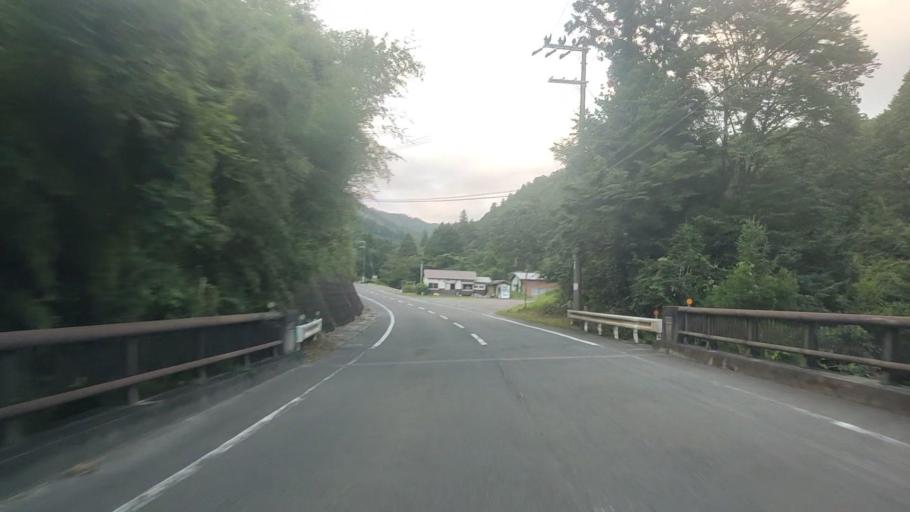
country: JP
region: Wakayama
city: Tanabe
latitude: 33.8271
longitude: 135.6385
